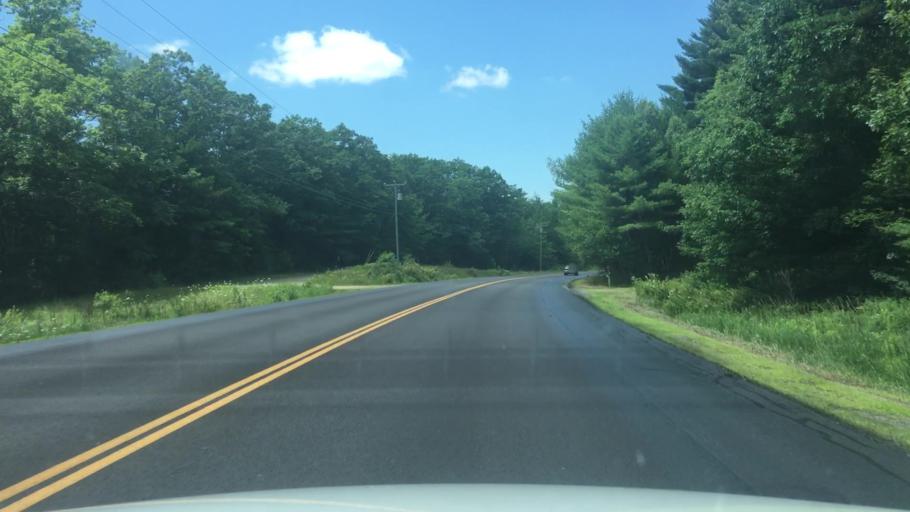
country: US
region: Maine
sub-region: Waldo County
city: Searsmont
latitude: 44.4061
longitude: -69.1968
